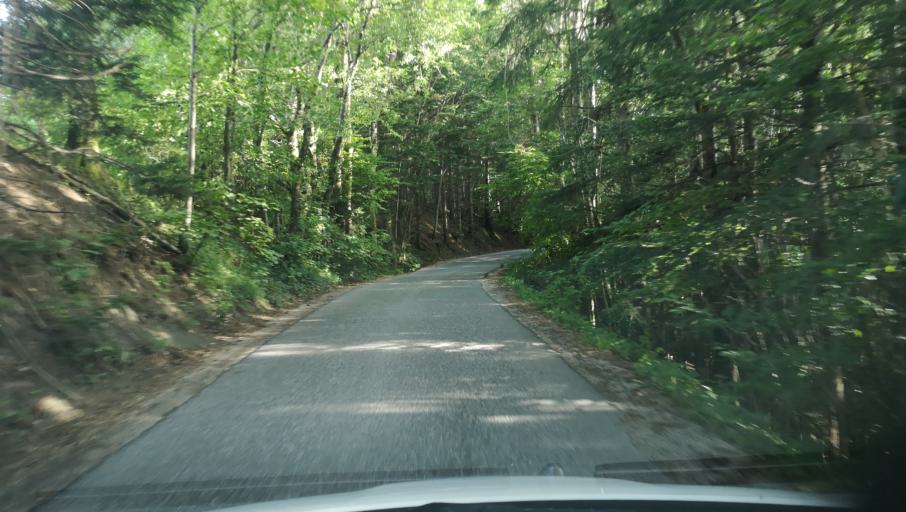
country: AT
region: Lower Austria
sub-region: Politischer Bezirk Amstetten
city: Euratsfeld
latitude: 48.0331
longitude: 14.9260
